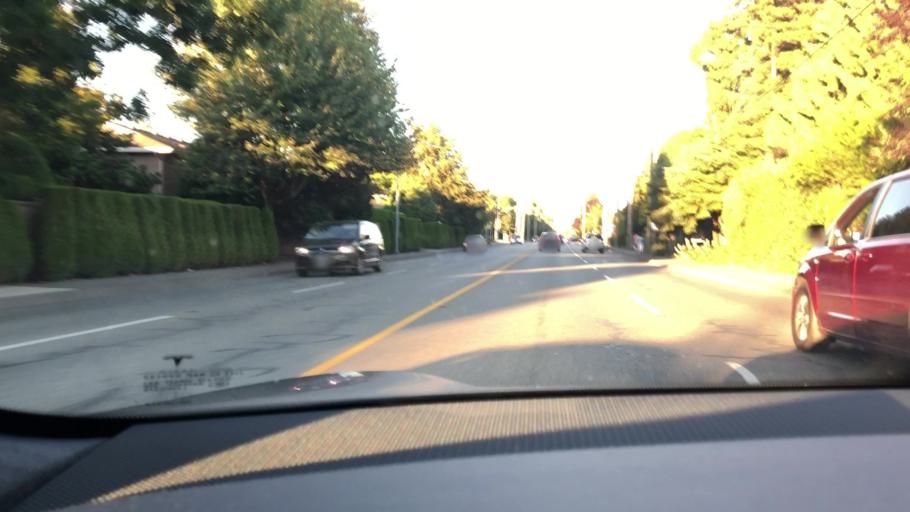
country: CA
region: British Columbia
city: Richmond
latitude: 49.1556
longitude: -123.1391
